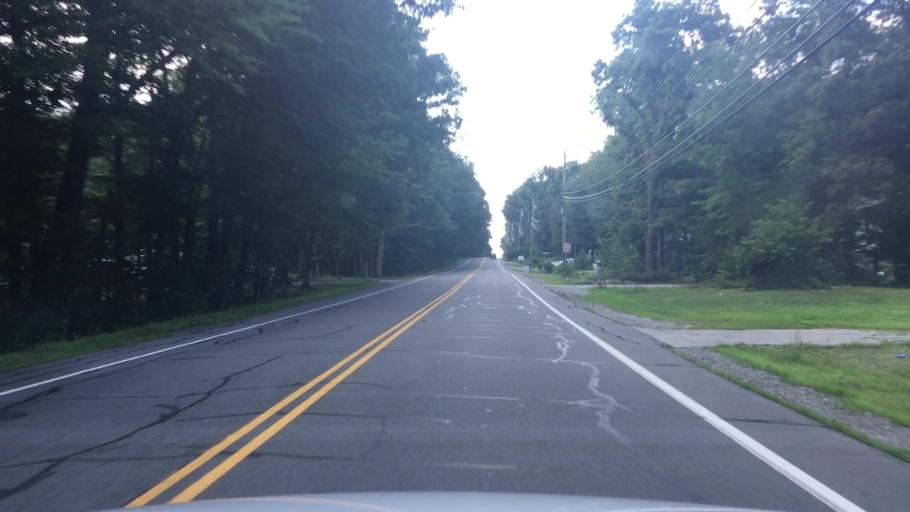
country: US
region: New Hampshire
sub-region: Rockingham County
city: Derry Village
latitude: 42.9219
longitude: -71.3339
